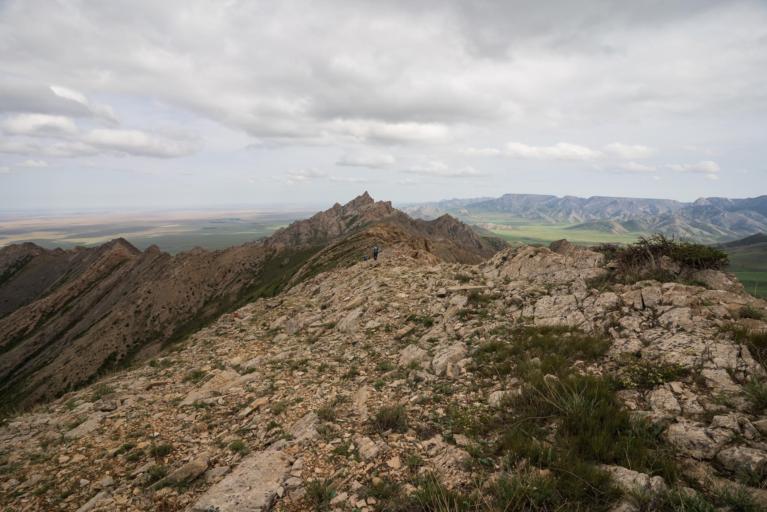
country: KZ
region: Ongtustik Qazaqstan
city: Ashchysay
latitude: 43.7545
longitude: 68.8172
